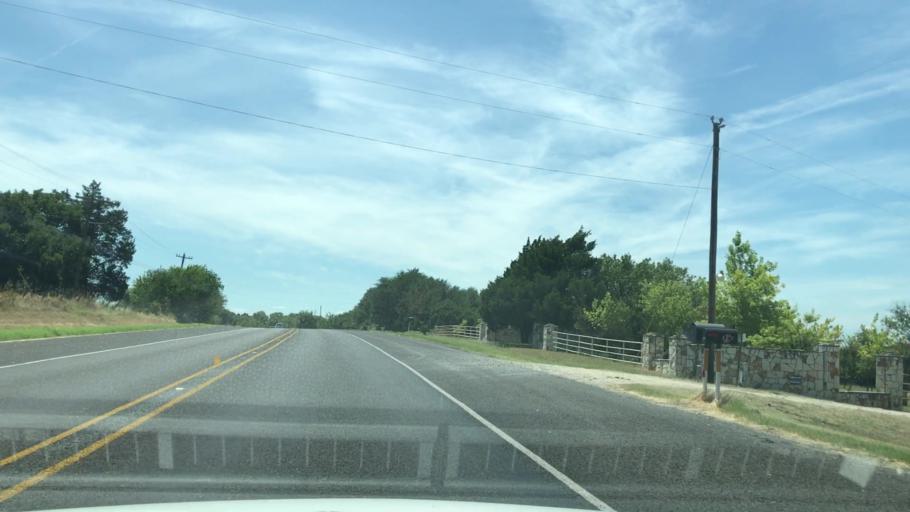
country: US
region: Texas
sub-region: Collin County
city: Lavon
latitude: 32.9959
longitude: -96.4662
